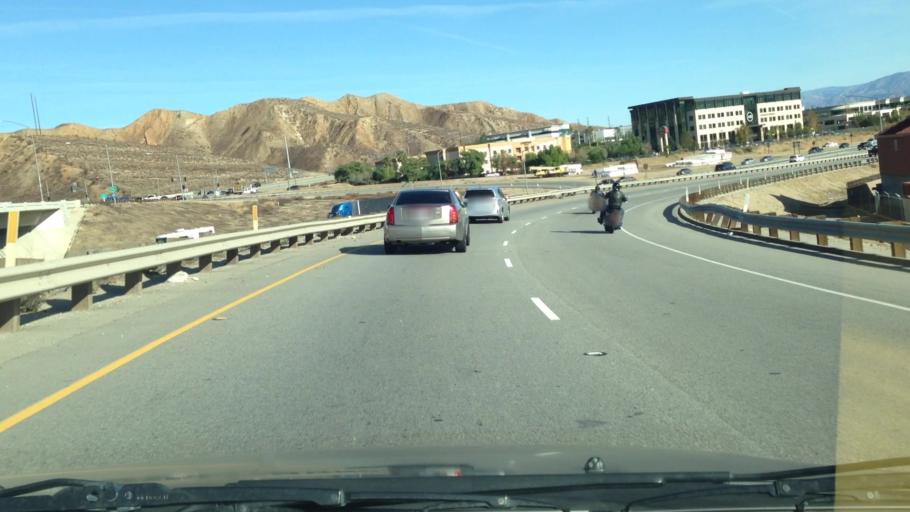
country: US
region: California
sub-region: Los Angeles County
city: Valencia
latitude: 34.4425
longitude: -118.6061
